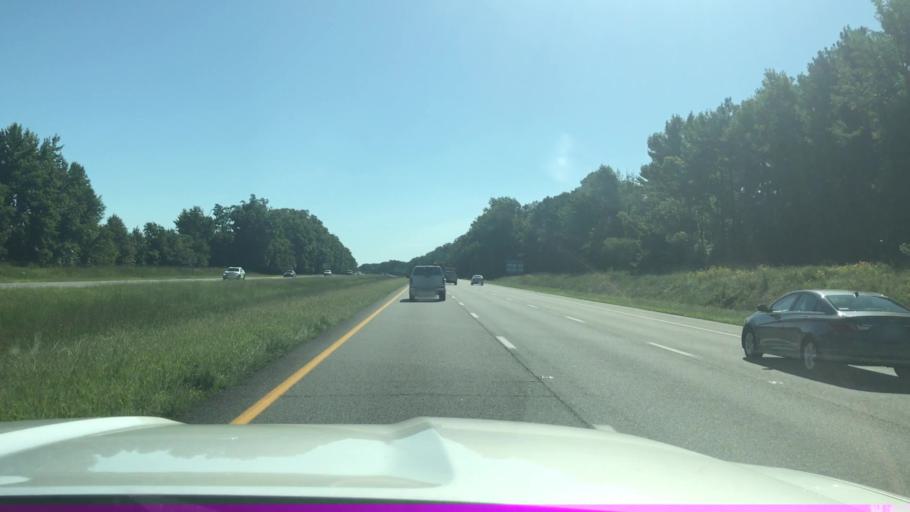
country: US
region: Virginia
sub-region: Henrico County
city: Highland Springs
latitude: 37.5310
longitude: -77.3420
